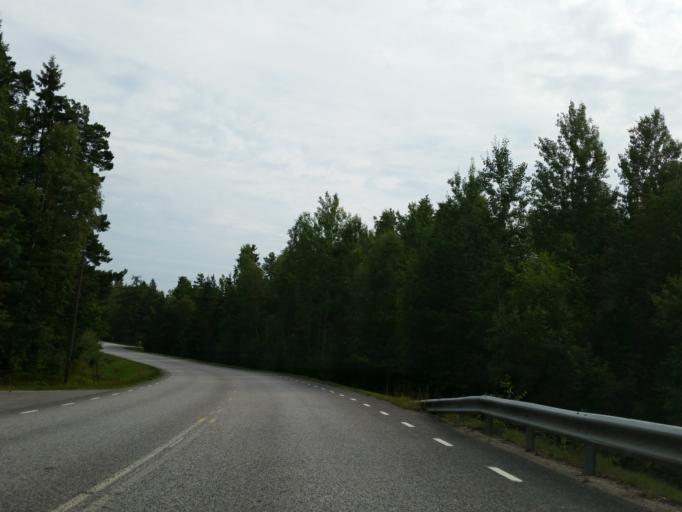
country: SE
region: Soedermanland
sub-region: Strangnas Kommun
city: Mariefred
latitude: 59.2272
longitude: 17.2153
